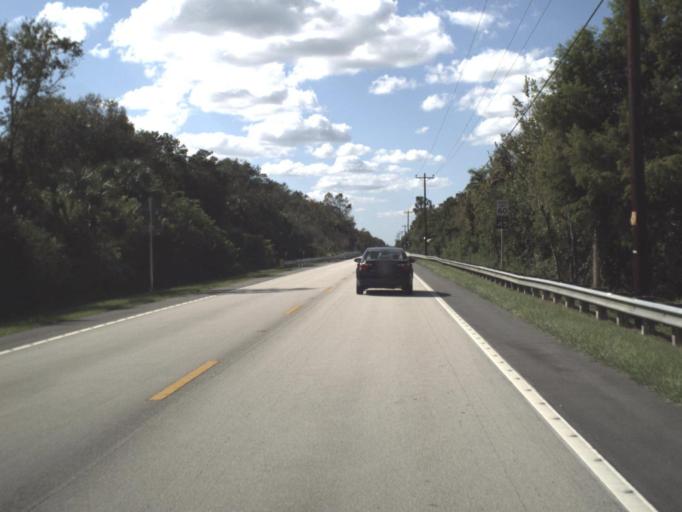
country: US
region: Florida
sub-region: Collier County
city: Marco
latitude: 25.8903
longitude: -81.2684
